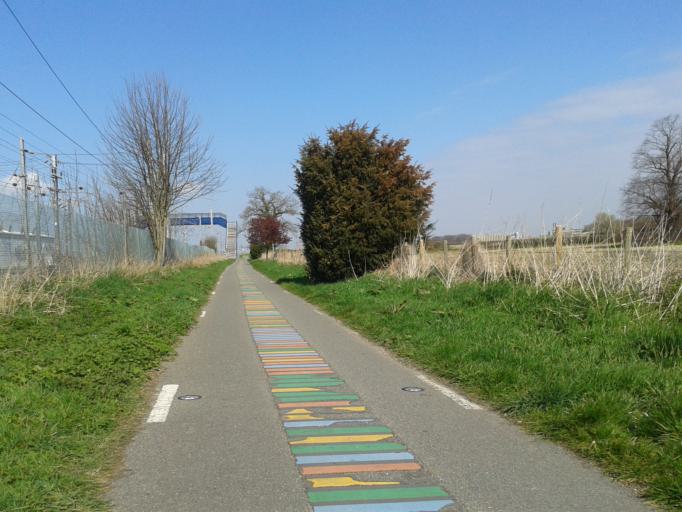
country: GB
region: England
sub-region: Cambridgeshire
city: Sawston
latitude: 52.1557
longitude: 0.1361
